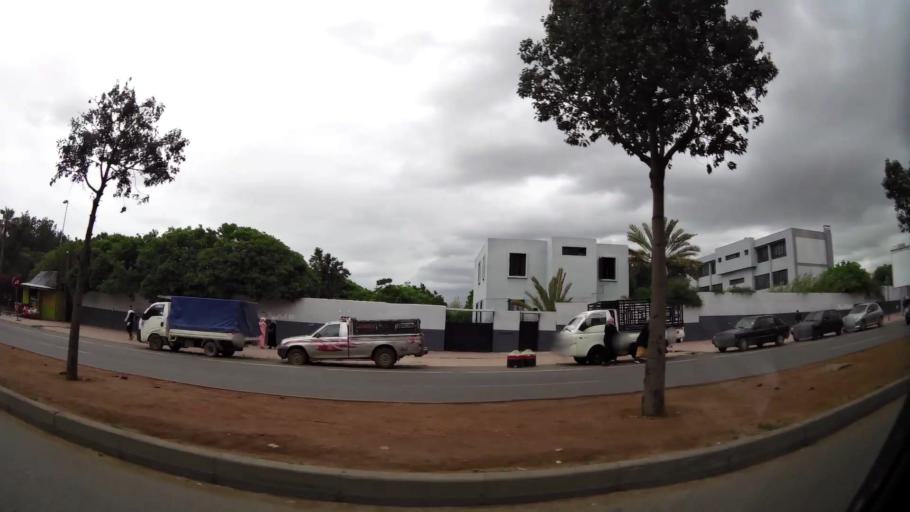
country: MA
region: Grand Casablanca
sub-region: Casablanca
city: Casablanca
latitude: 33.5634
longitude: -7.5541
